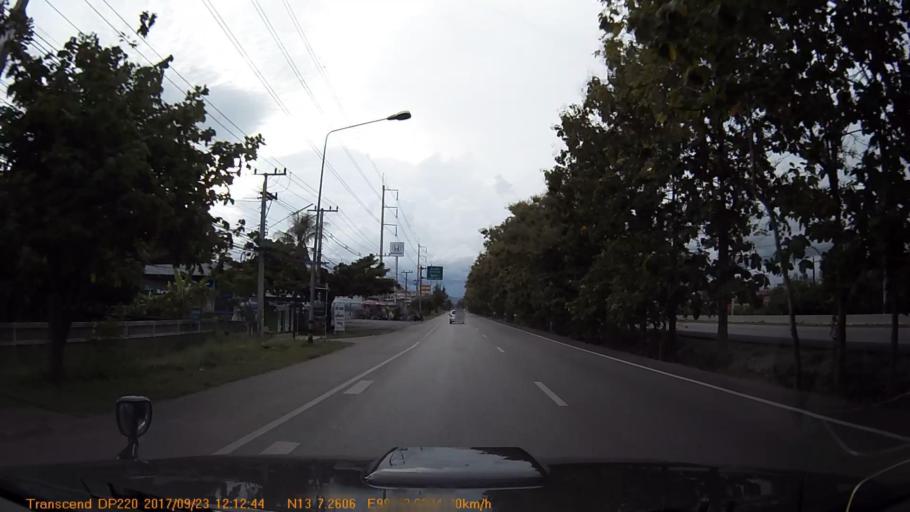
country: TH
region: Phetchaburi
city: Phetchaburi
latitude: 13.1210
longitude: 99.8938
